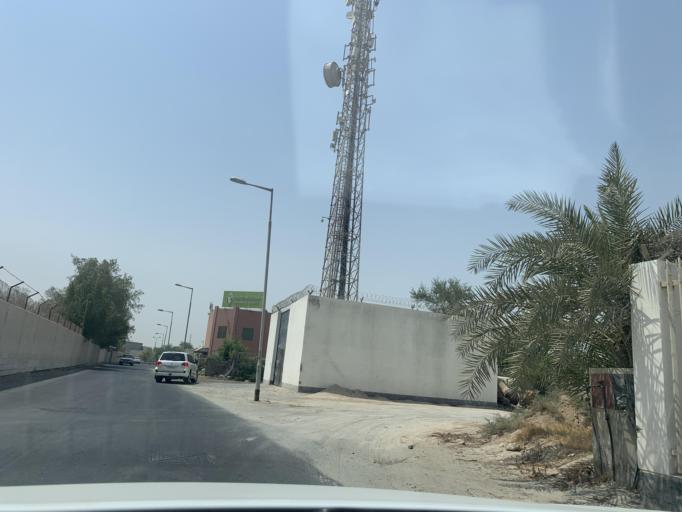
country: BH
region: Manama
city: Jidd Hafs
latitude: 26.2196
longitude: 50.5039
